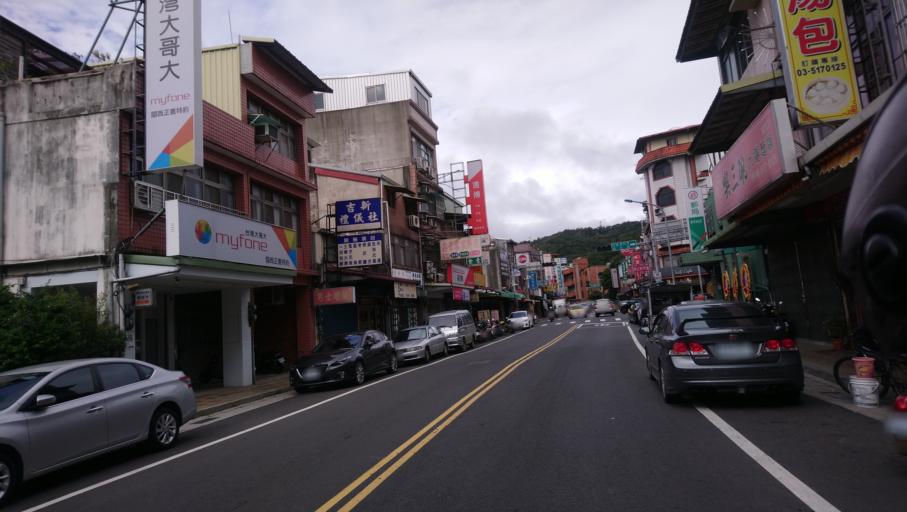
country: TW
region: Taiwan
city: Daxi
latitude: 24.7931
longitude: 121.1760
